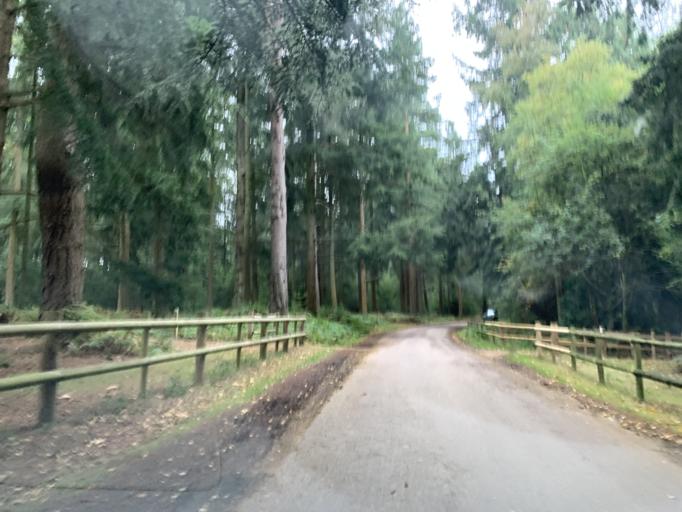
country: GB
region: England
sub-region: Hampshire
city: Lyndhurst
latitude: 50.8762
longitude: -1.6569
